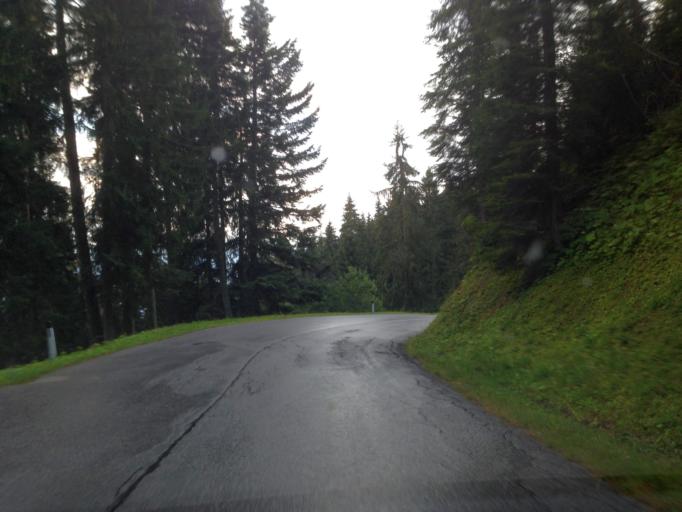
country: AT
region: Salzburg
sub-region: Politischer Bezirk Sankt Johann im Pongau
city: Filzmoos
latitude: 47.4348
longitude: 13.6044
